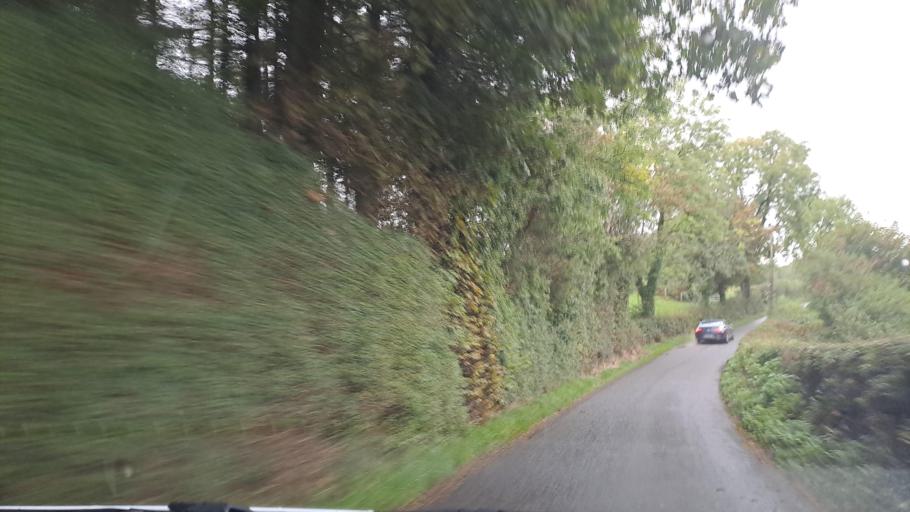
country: IE
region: Ulster
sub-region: County Monaghan
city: Monaghan
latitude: 54.2065
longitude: -6.9086
